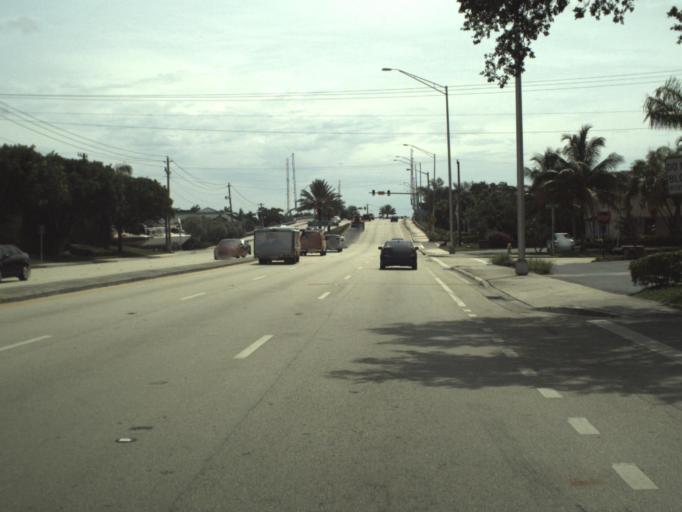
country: US
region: Florida
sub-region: Palm Beach County
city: North Palm Beach
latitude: 26.8445
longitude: -80.0696
